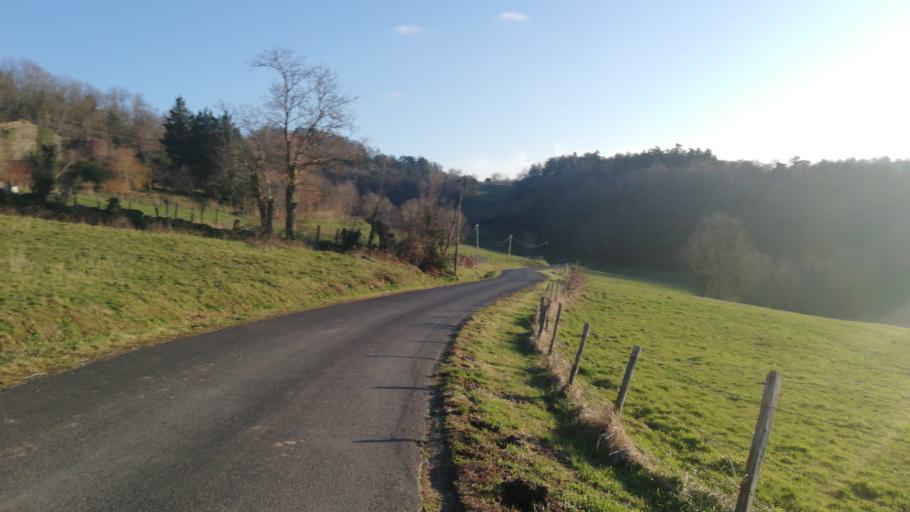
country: FR
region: Auvergne
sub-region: Departement du Puy-de-Dome
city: Billom
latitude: 45.6880
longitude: 3.3793
